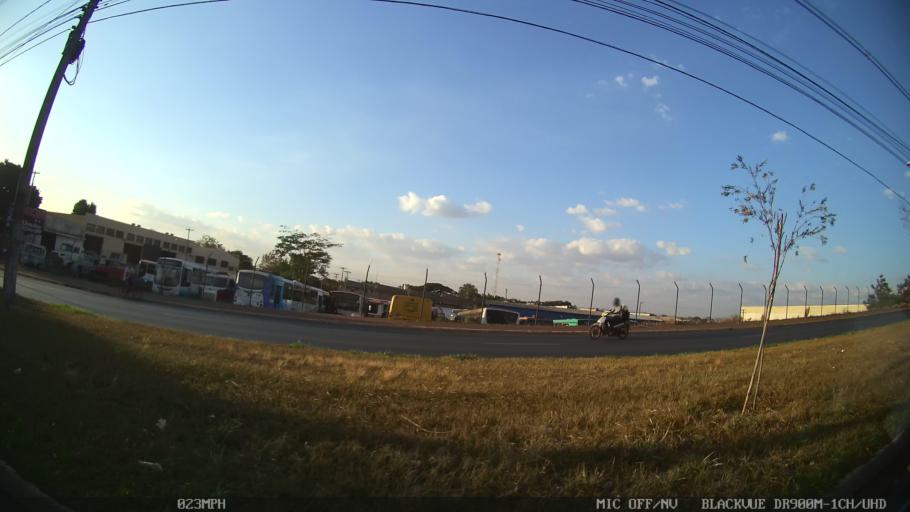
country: BR
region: Sao Paulo
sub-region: Ribeirao Preto
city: Ribeirao Preto
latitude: -21.1384
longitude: -47.7942
